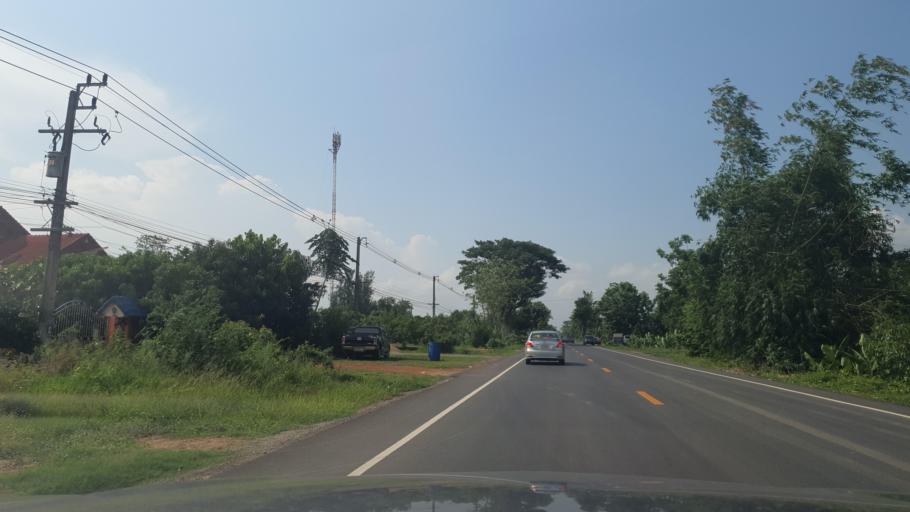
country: TH
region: Sukhothai
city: Si Samrong
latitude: 17.2083
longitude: 99.8493
